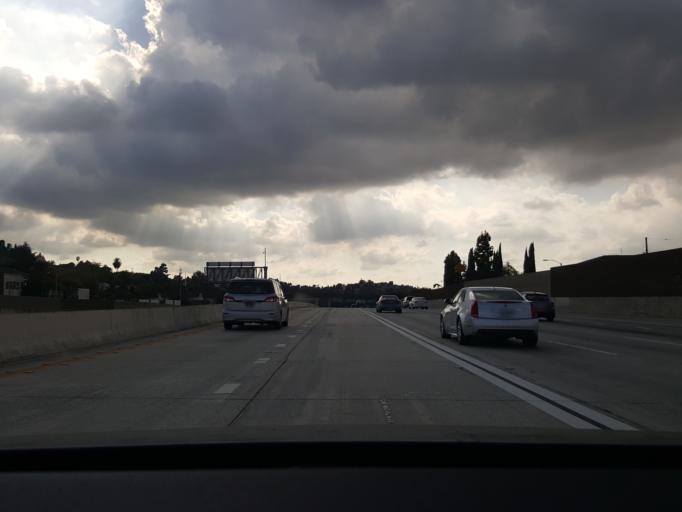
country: US
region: California
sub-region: Los Angeles County
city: Belvedere
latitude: 34.0666
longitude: -118.1547
